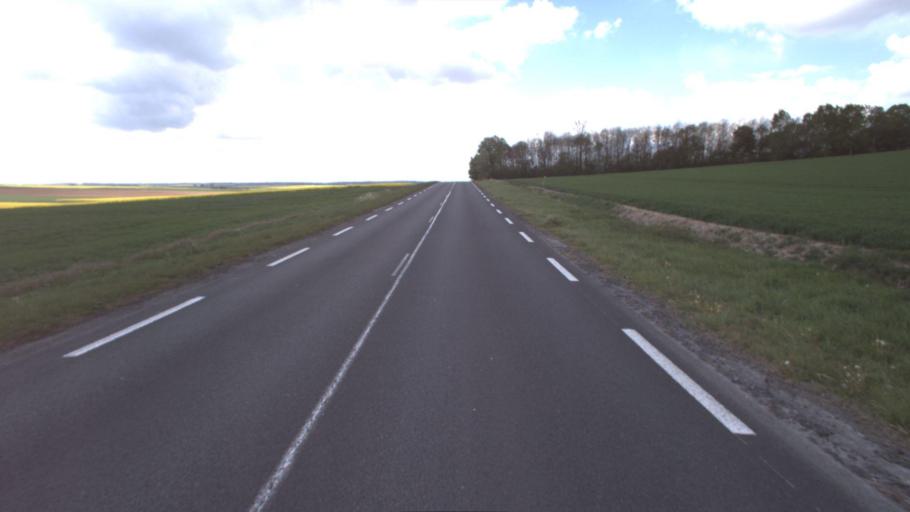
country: FR
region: Ile-de-France
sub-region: Departement de Seine-et-Marne
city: Villiers-Saint-Georges
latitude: 48.6921
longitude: 3.4159
